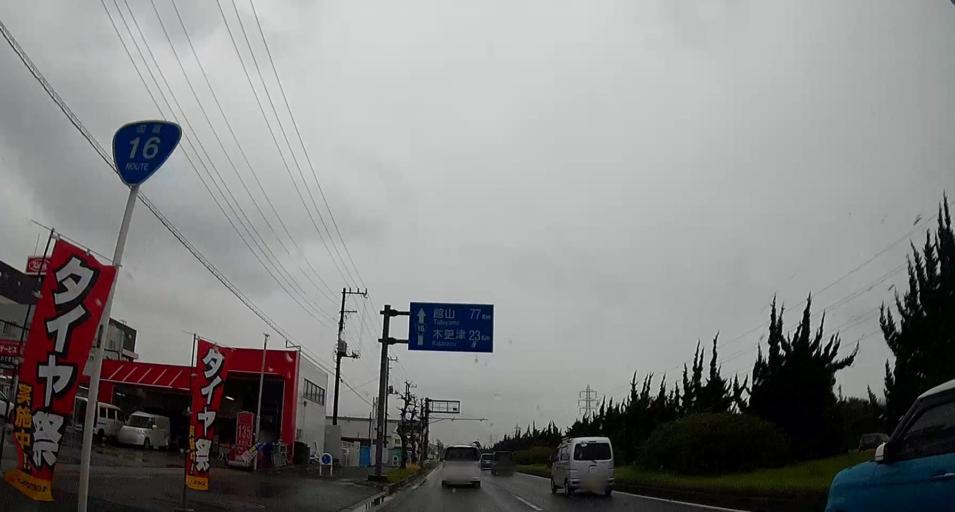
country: JP
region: Chiba
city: Ichihara
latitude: 35.5188
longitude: 140.0612
